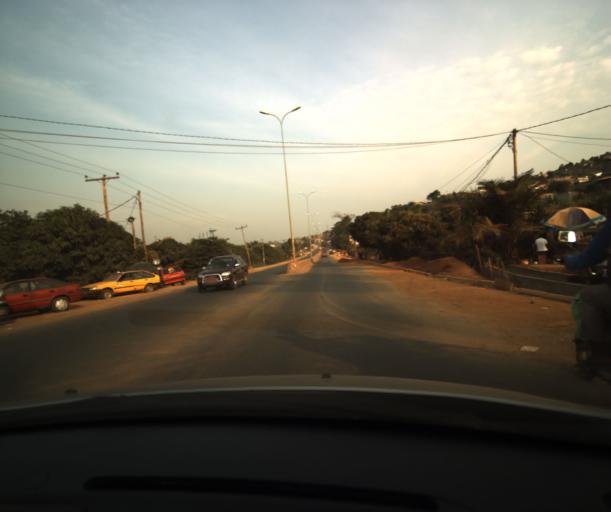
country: CM
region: Centre
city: Yaounde
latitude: 3.8712
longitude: 11.4756
